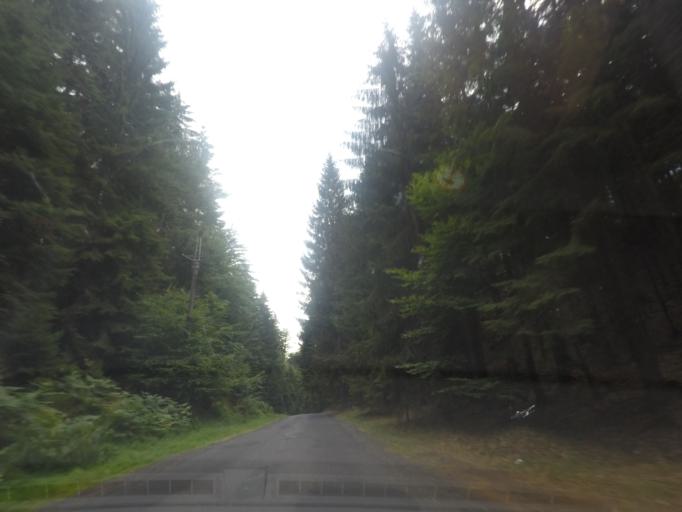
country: CZ
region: Ustecky
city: Ceska Kamenice
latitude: 50.8512
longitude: 14.4081
